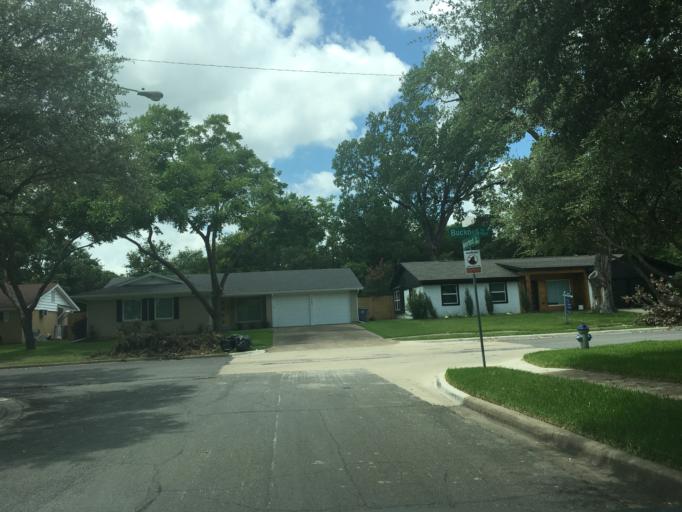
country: US
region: Texas
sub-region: Dallas County
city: Highland Park
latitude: 32.8526
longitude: -96.7420
